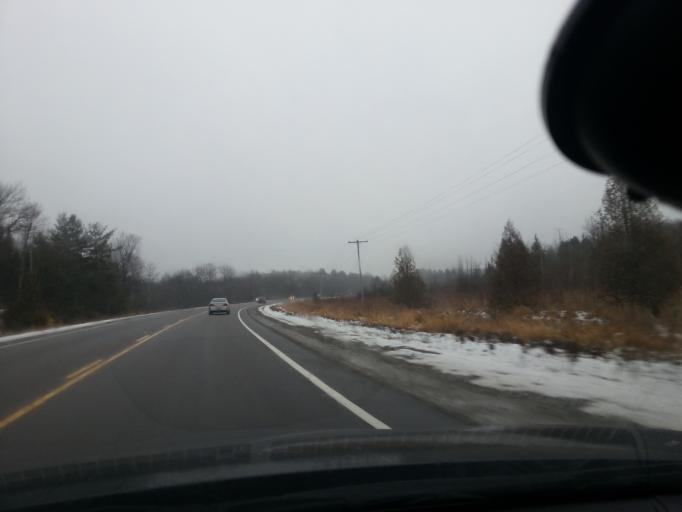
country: CA
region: Ontario
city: Skatepark
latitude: 44.7546
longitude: -76.8943
